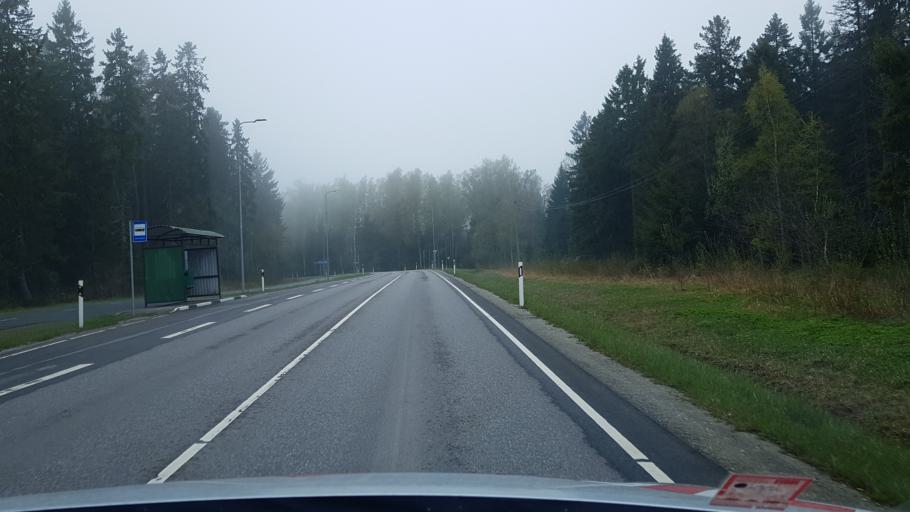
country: EE
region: Harju
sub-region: Viimsi vald
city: Viimsi
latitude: 59.5206
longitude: 24.8963
